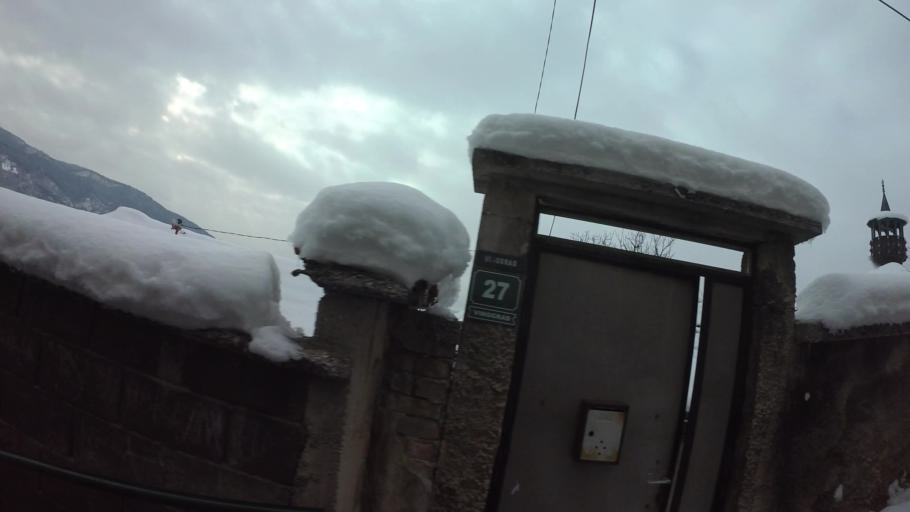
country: BA
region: Federation of Bosnia and Herzegovina
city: Kobilja Glava
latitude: 43.8678
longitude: 18.4371
